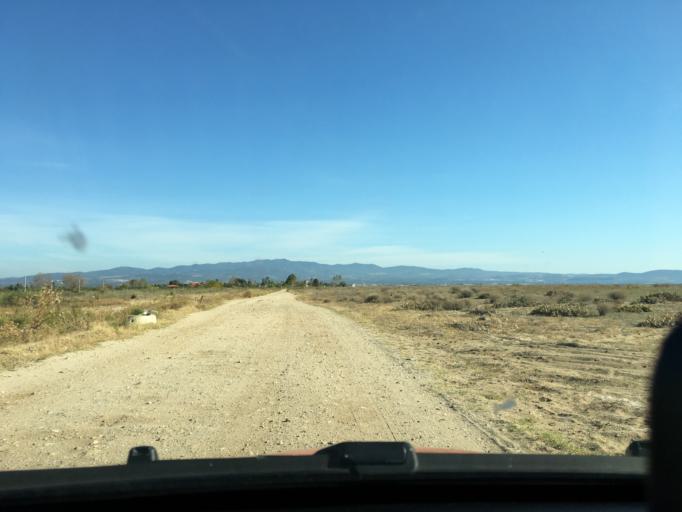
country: GR
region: Central Macedonia
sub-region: Nomos Chalkidikis
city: Nea Potidhaia
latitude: 40.2375
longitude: 23.3459
